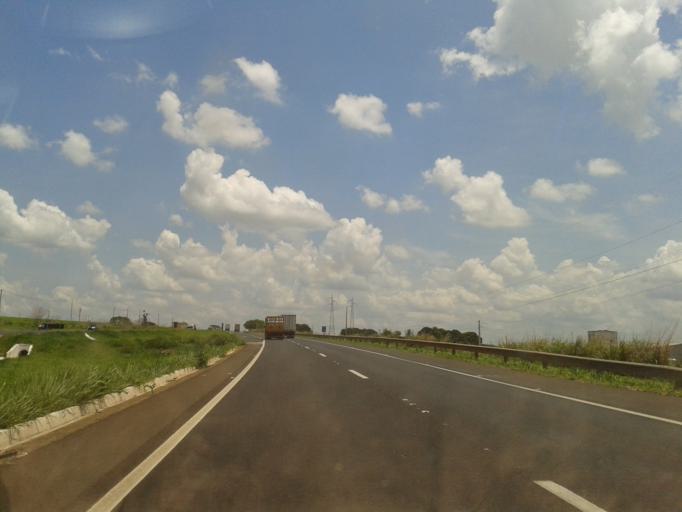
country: BR
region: Minas Gerais
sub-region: Uberlandia
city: Uberlandia
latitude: -18.8687
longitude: -48.5601
